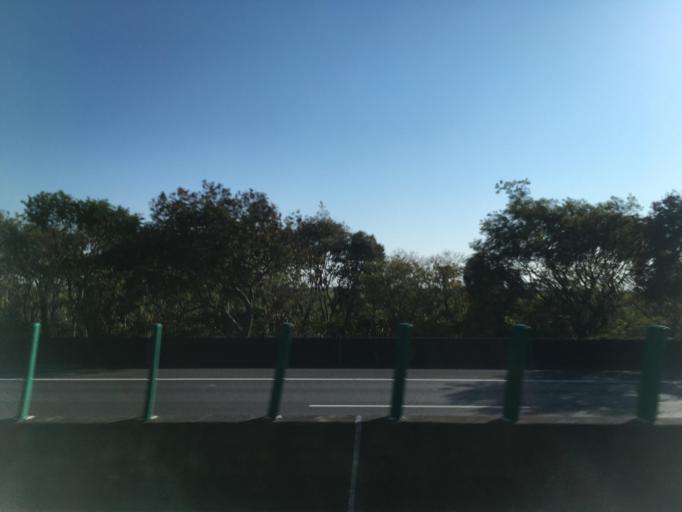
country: TW
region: Taiwan
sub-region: Chiayi
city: Taibao
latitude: 23.4283
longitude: 120.3347
